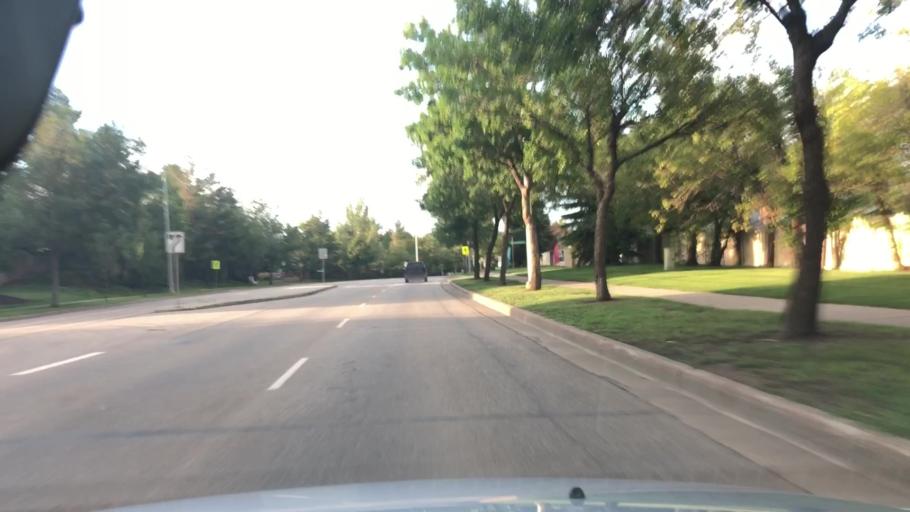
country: CA
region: Alberta
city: St. Albert
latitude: 53.6479
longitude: -113.6205
